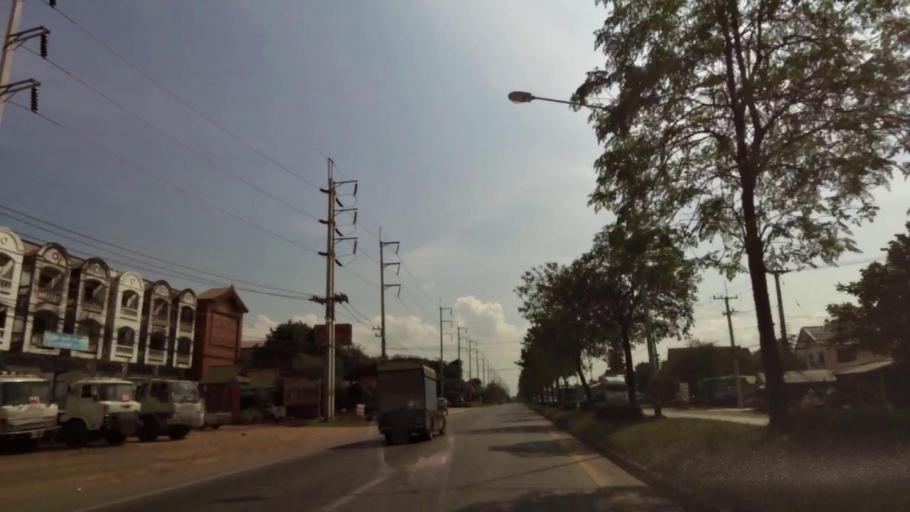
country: TH
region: Uttaradit
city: Uttaradit
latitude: 17.5940
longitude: 100.1303
